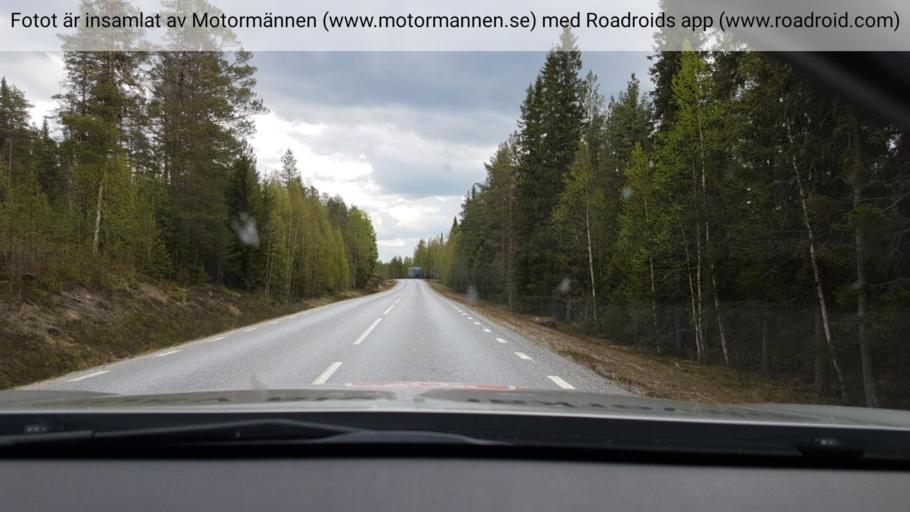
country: SE
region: Vaesterbotten
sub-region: Bjurholms Kommun
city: Bjurholm
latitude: 64.0030
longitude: 18.7305
